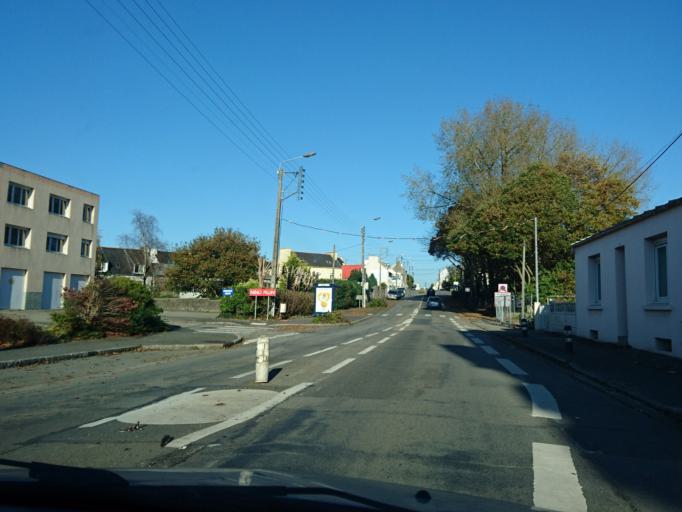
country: FR
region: Brittany
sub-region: Departement du Finistere
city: Brest
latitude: 48.4106
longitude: -4.4548
